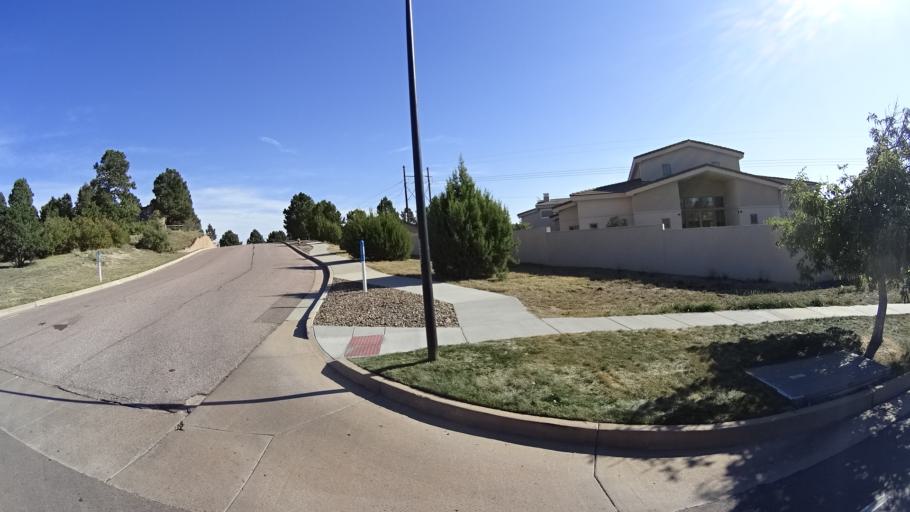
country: US
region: Colorado
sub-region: El Paso County
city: Colorado Springs
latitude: 38.9106
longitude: -104.7902
